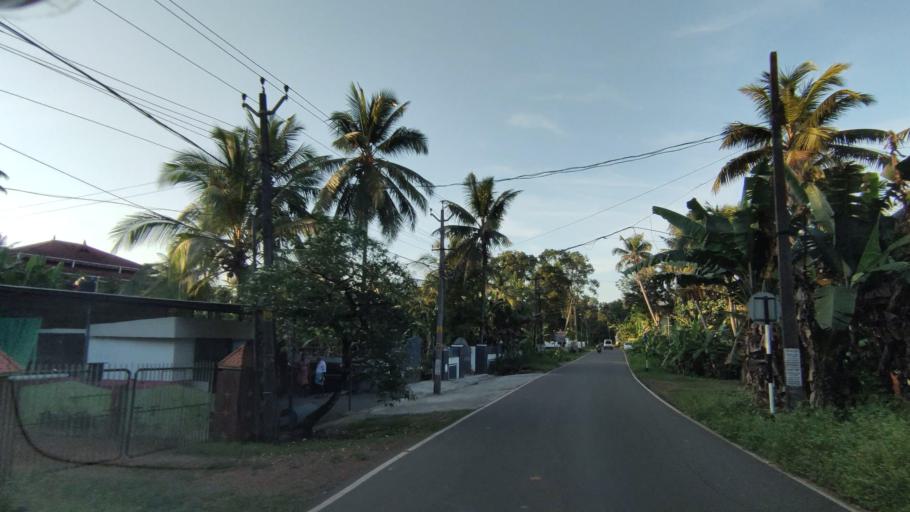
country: IN
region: Kerala
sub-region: Kottayam
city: Kottayam
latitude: 9.6243
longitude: 76.4915
